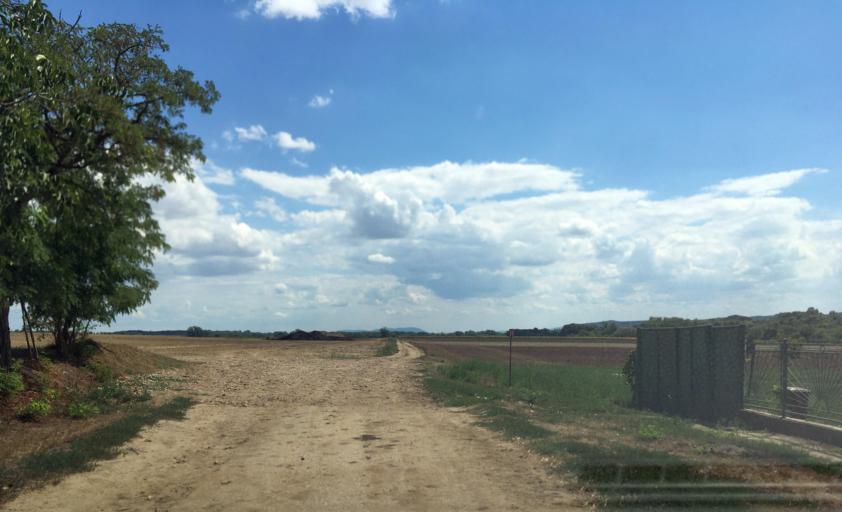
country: SK
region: Nitriansky
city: Svodin
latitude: 47.8978
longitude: 18.4281
